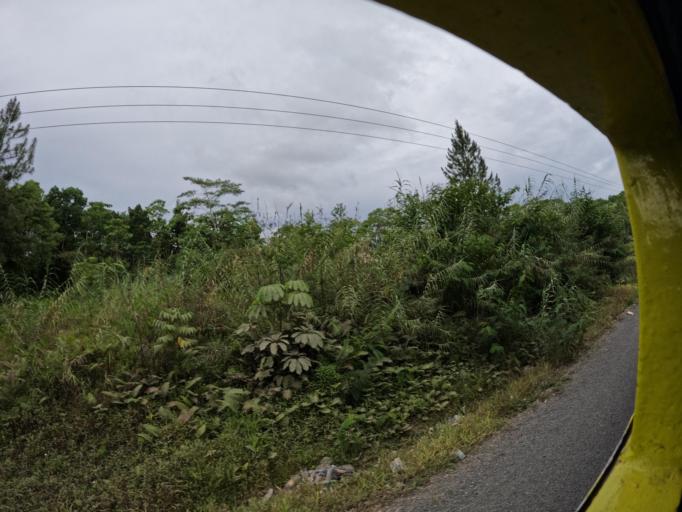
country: FJ
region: Central
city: Suva
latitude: -18.0661
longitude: 178.4597
